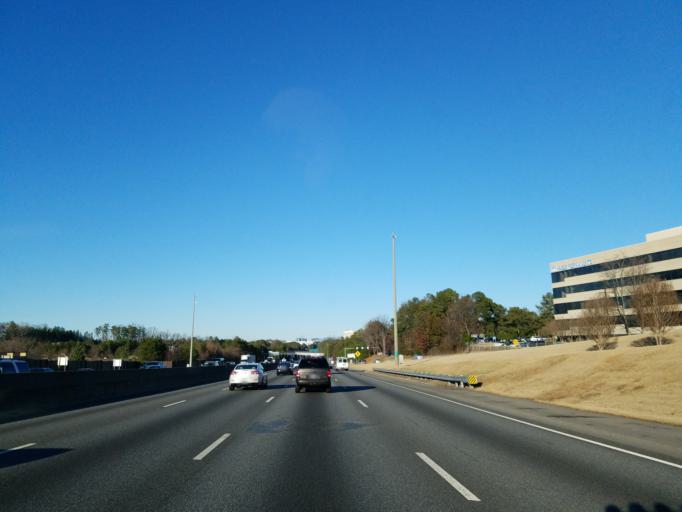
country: US
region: Georgia
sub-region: Cobb County
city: Vinings
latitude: 33.8663
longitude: -84.4786
